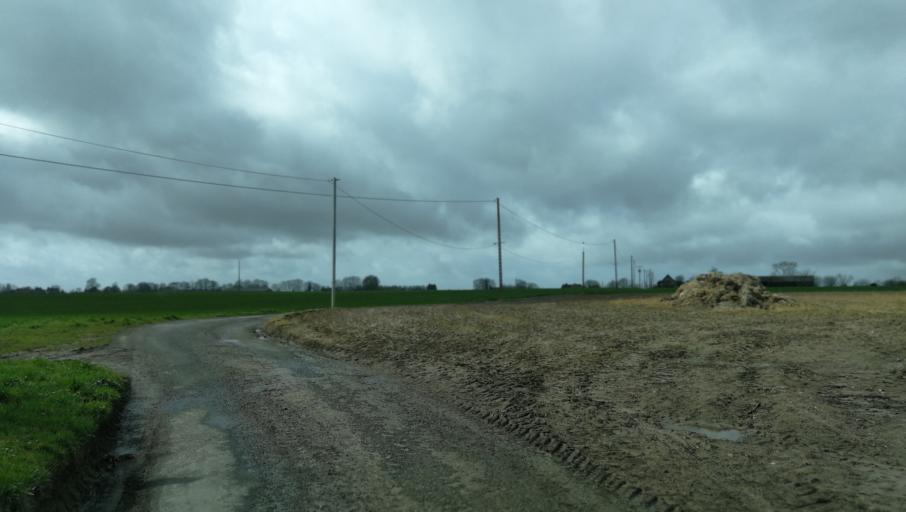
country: FR
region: Haute-Normandie
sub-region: Departement de l'Eure
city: Lieurey
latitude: 49.2328
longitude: 0.5353
